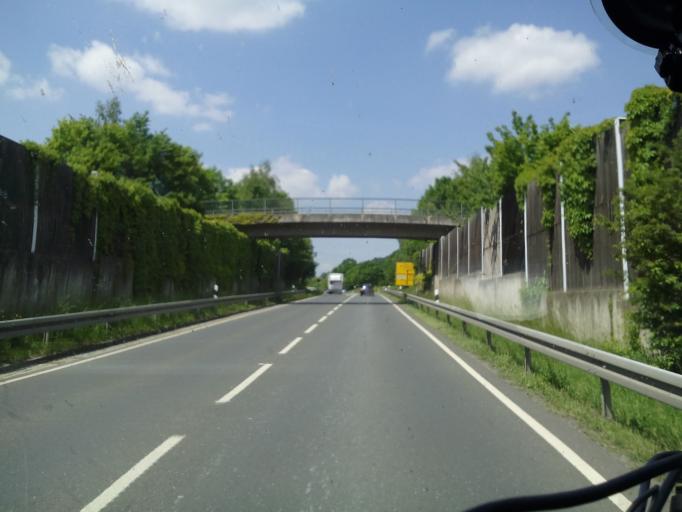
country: DE
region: Bavaria
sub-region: Upper Franconia
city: Mainleus
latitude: 50.1028
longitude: 11.3894
